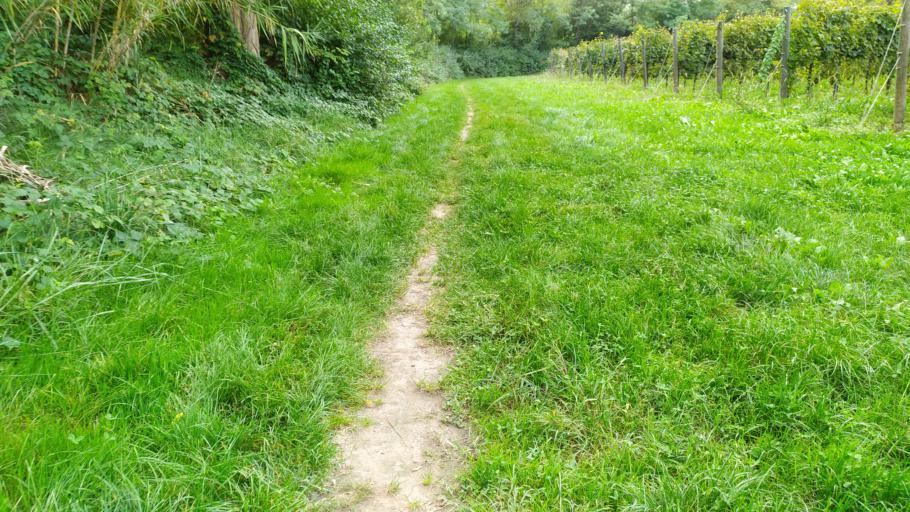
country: IT
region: Veneto
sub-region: Provincia di Treviso
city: Conegliano
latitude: 45.9017
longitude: 12.2957
